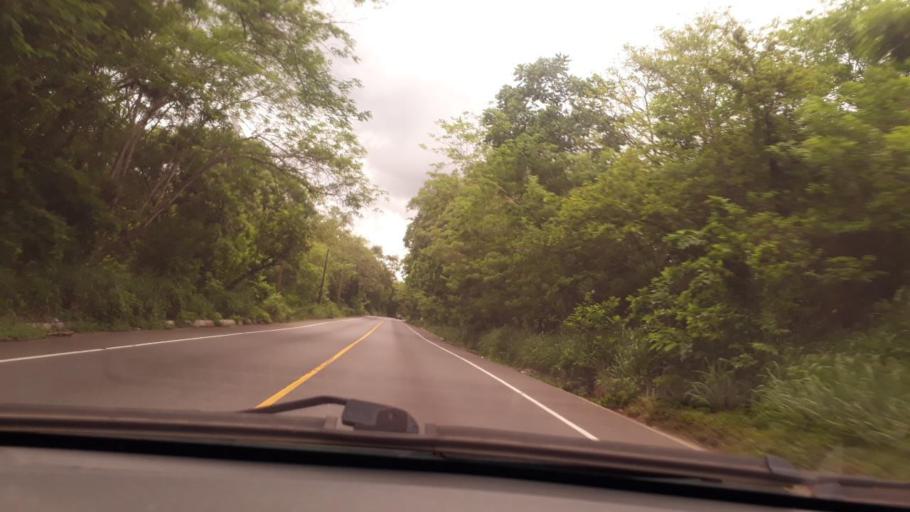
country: GT
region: Izabal
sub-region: Municipio de Los Amates
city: Los Amates
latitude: 15.2167
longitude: -89.2279
